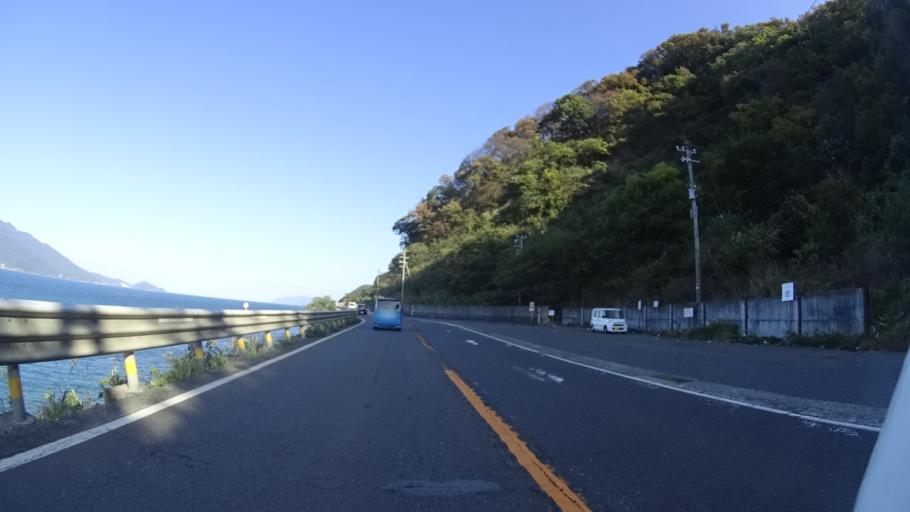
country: JP
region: Fukui
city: Tsuruga
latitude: 35.6896
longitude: 136.0817
